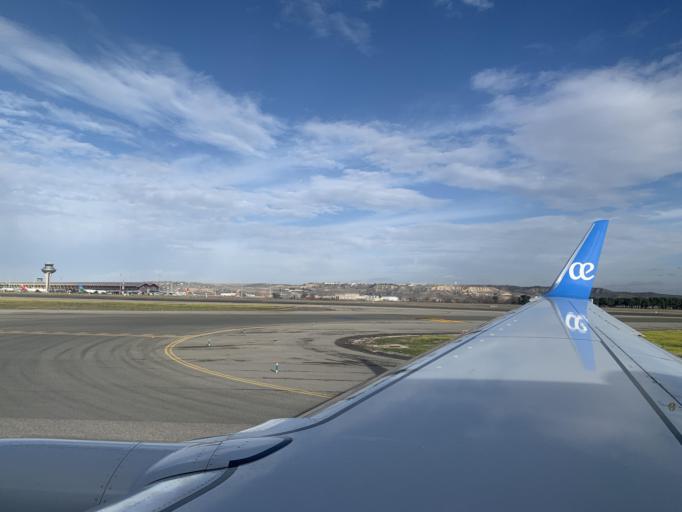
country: ES
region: Madrid
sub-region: Provincia de Madrid
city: Barajas de Madrid
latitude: 40.4811
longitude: -3.5749
